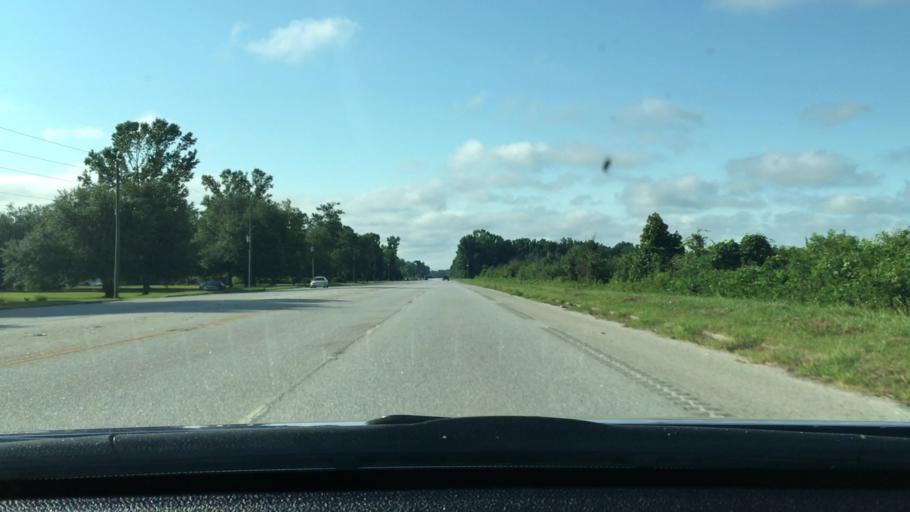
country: US
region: South Carolina
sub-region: Clarendon County
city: Manning
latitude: 33.7655
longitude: -80.2325
